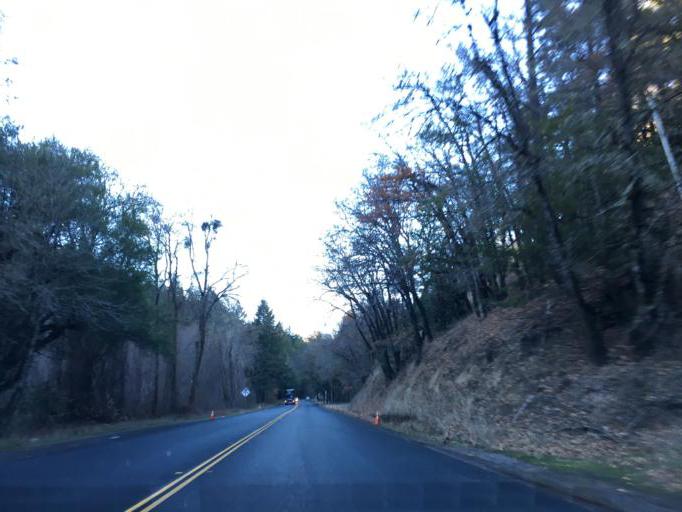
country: US
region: California
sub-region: Mendocino County
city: Laytonville
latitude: 39.8115
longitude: -123.5565
